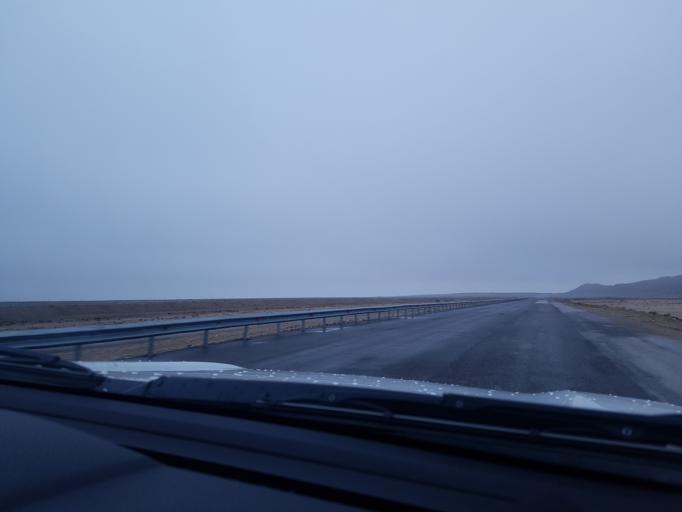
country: TM
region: Balkan
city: Balkanabat
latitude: 39.9111
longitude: 53.9168
